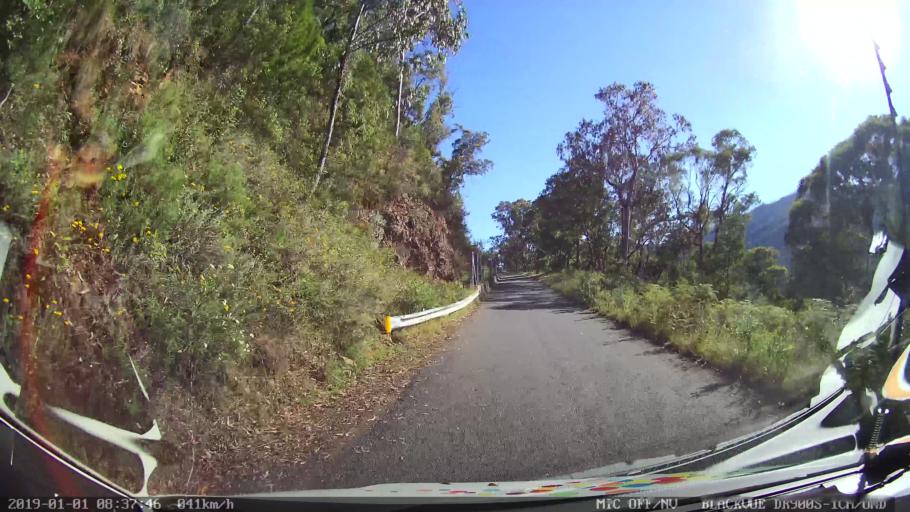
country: AU
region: New South Wales
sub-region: Snowy River
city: Jindabyne
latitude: -36.3363
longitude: 148.1966
